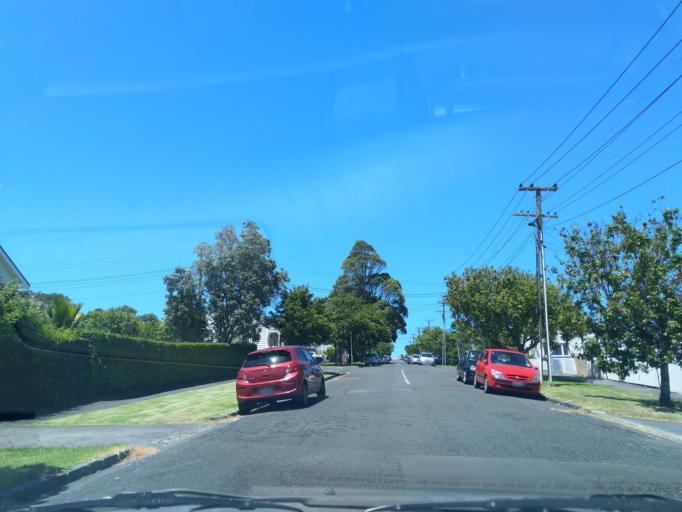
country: NZ
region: Auckland
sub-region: Auckland
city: Auckland
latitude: -36.8703
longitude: 174.7412
